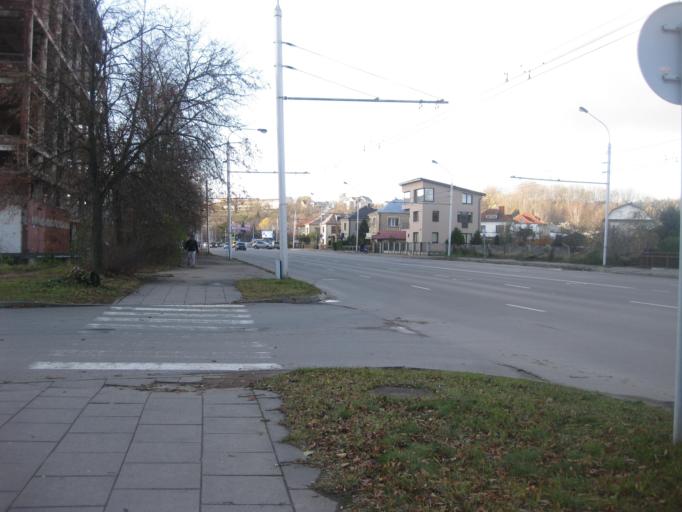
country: LT
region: Kauno apskritis
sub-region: Kaunas
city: Kaunas
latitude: 54.9148
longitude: 23.8956
